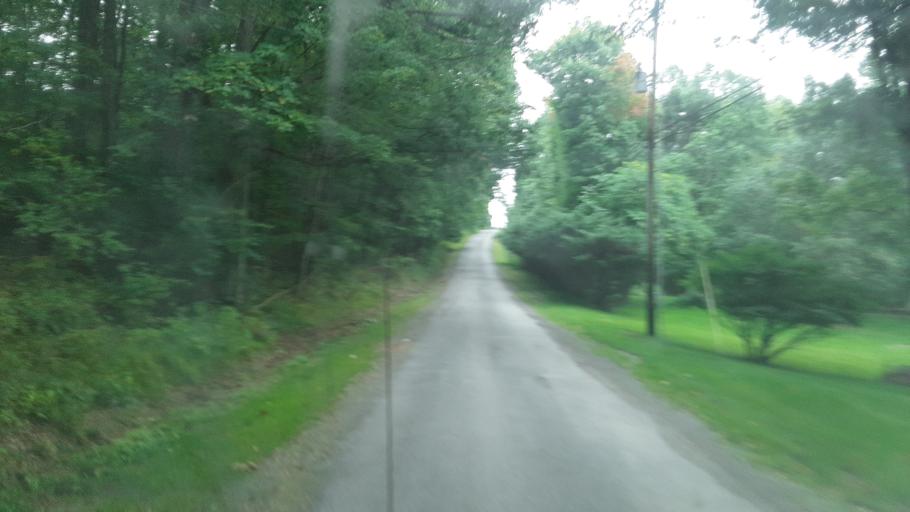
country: US
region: Pennsylvania
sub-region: Jefferson County
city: Punxsutawney
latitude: 40.9616
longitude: -79.1224
